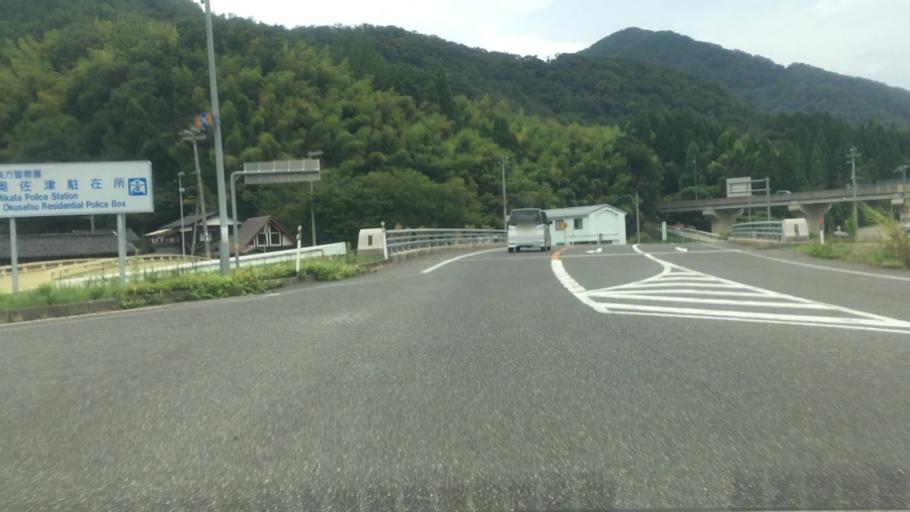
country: JP
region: Hyogo
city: Toyooka
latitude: 35.6271
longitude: 134.6787
